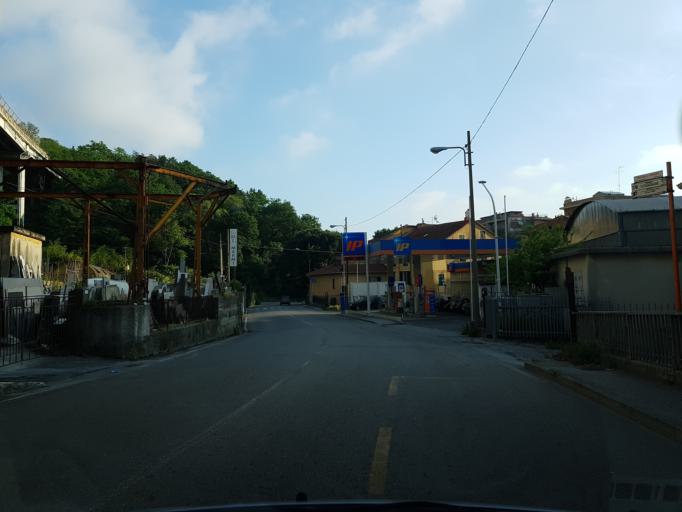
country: IT
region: Liguria
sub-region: Provincia di Genova
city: Genoa
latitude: 44.4423
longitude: 8.9038
